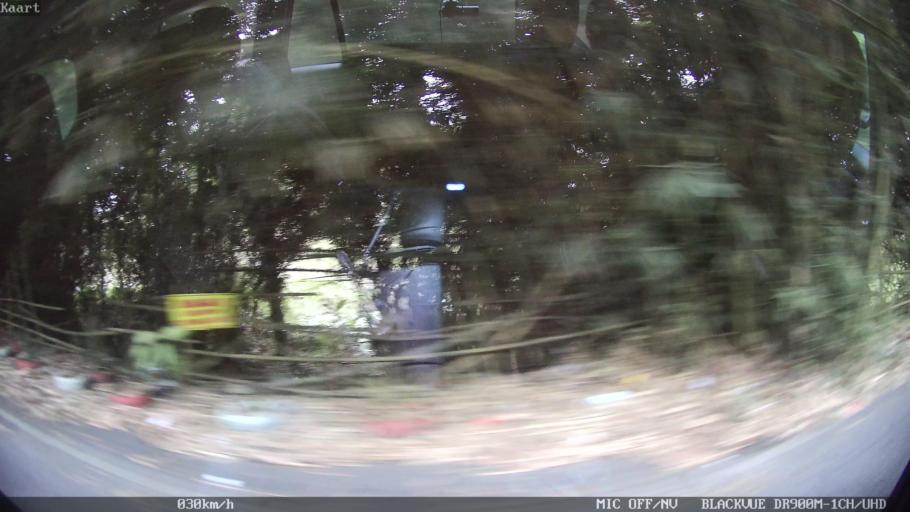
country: ID
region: Lampung
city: Bandarlampung
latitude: -5.4218
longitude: 105.2353
